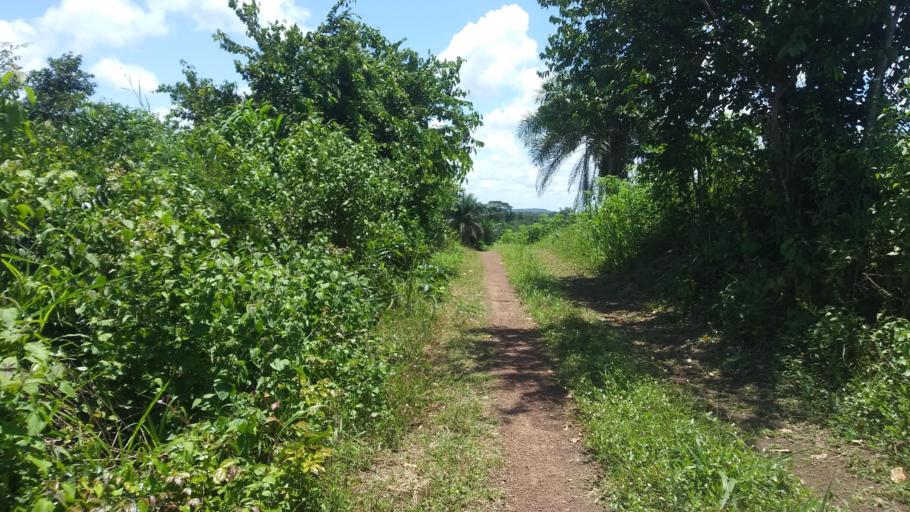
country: SL
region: Northern Province
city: Binkolo
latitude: 8.9100
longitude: -11.9779
